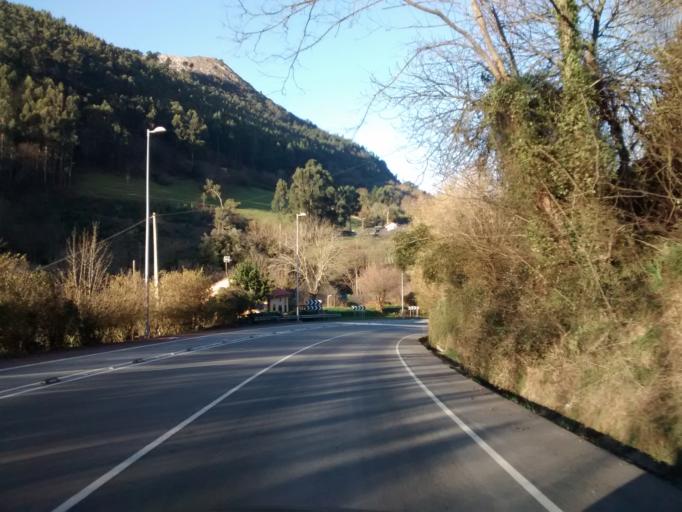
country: ES
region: Cantabria
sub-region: Provincia de Cantabria
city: Lierganes
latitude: 43.3893
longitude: -3.7588
